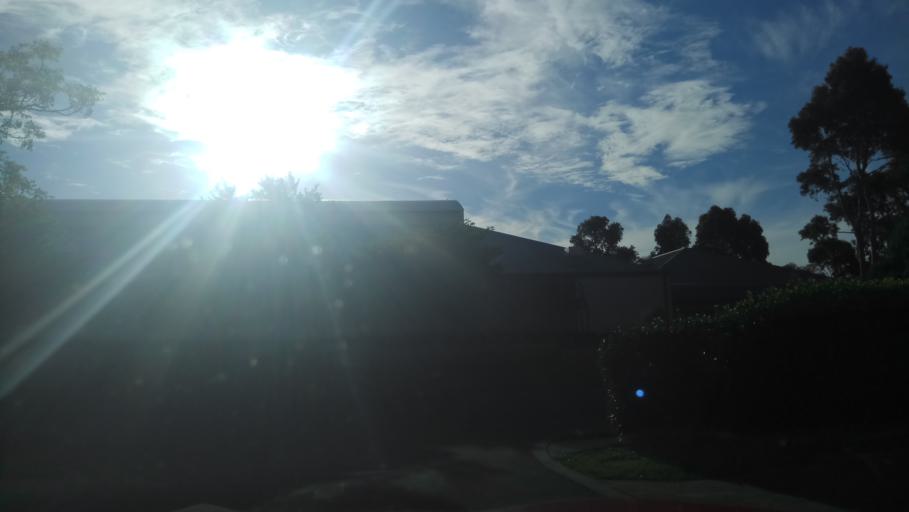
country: AU
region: Victoria
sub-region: Hobsons Bay
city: Williamstown North
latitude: -37.8578
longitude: 144.8832
